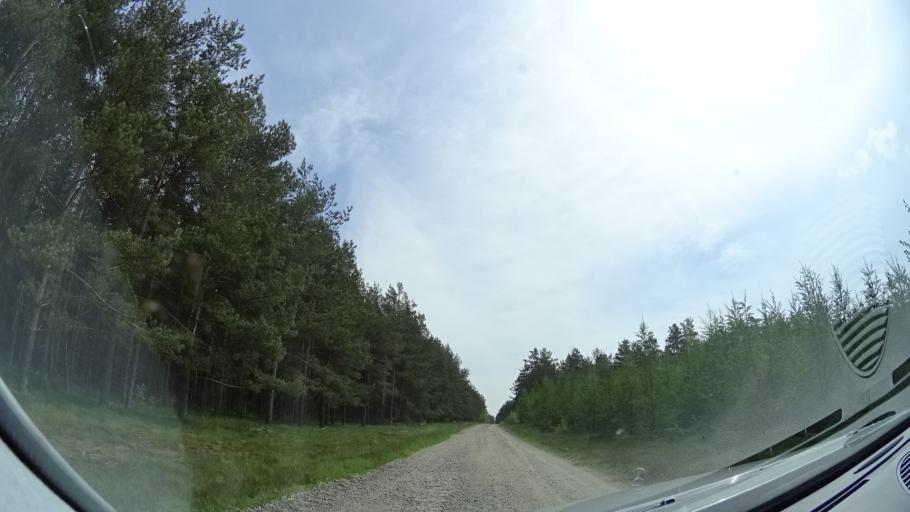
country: SE
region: Skane
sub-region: Sjobo Kommun
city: Sjoebo
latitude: 55.6720
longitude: 13.6324
